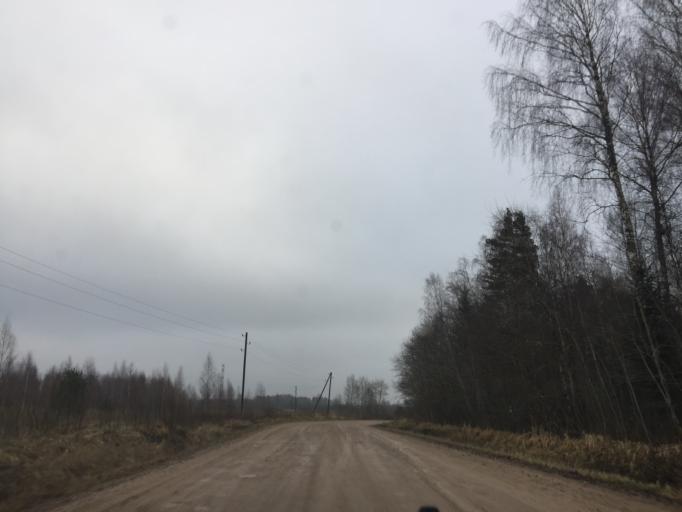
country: LV
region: Limbazu Rajons
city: Limbazi
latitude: 57.5862
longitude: 24.6547
